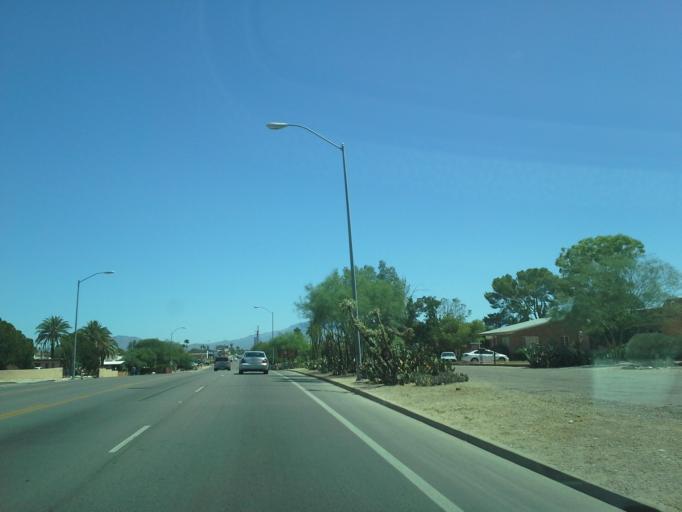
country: US
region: Arizona
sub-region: Pima County
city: Tucson
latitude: 32.2502
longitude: -110.9403
